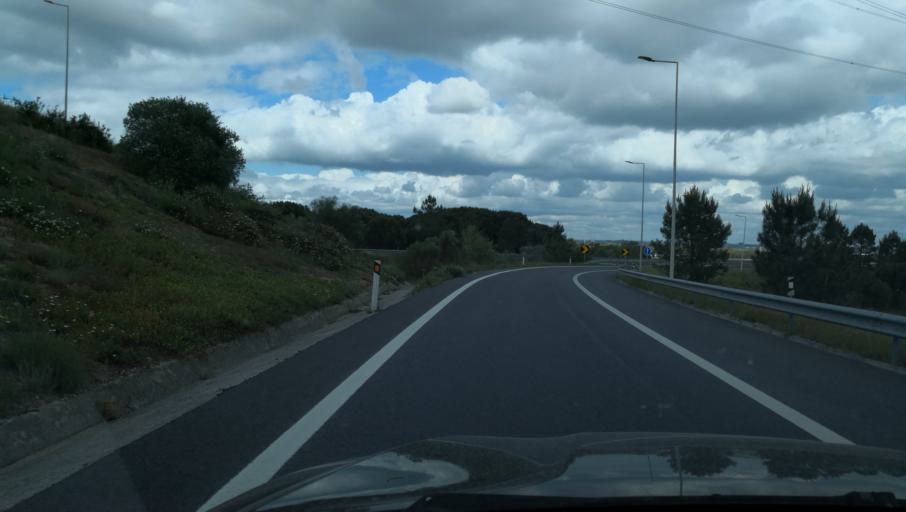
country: PT
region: Setubal
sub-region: Palmela
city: Palmela
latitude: 38.5807
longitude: -8.8613
